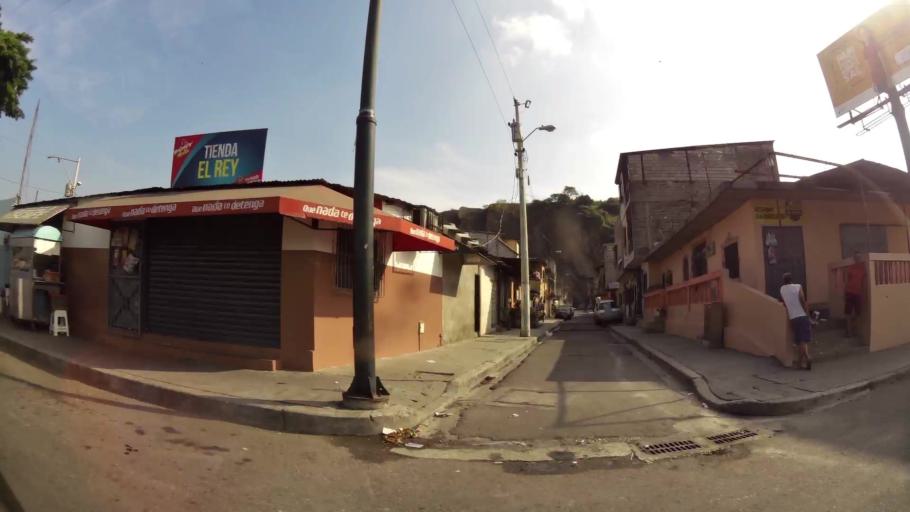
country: EC
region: Guayas
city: Guayaquil
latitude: -2.1880
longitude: -79.9077
